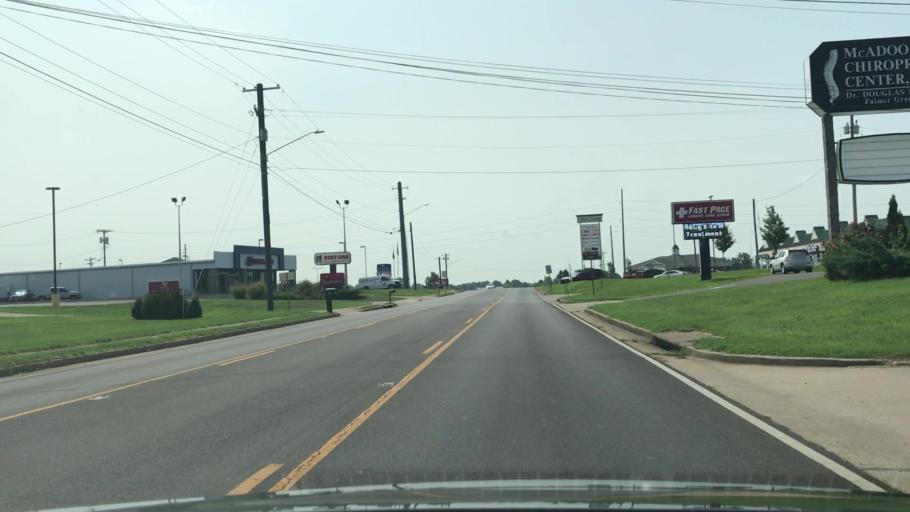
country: US
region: Kentucky
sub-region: Graves County
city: Mayfield
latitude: 36.7204
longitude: -88.6261
